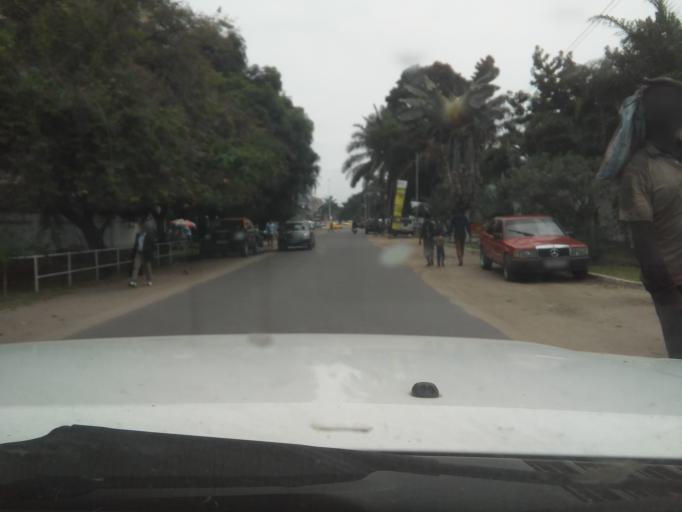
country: CD
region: Kinshasa
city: Kinshasa
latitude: -4.3132
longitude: 15.2871
